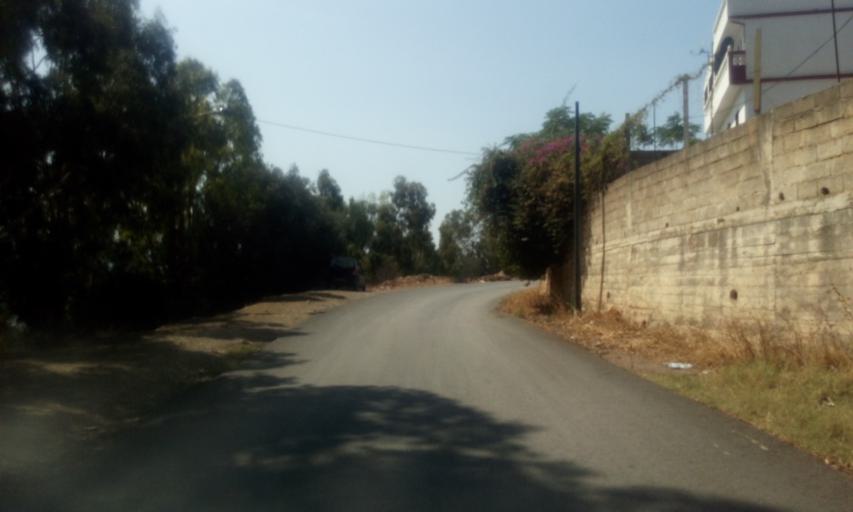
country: DZ
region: Bejaia
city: Bejaia
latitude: 36.7616
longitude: 5.0887
